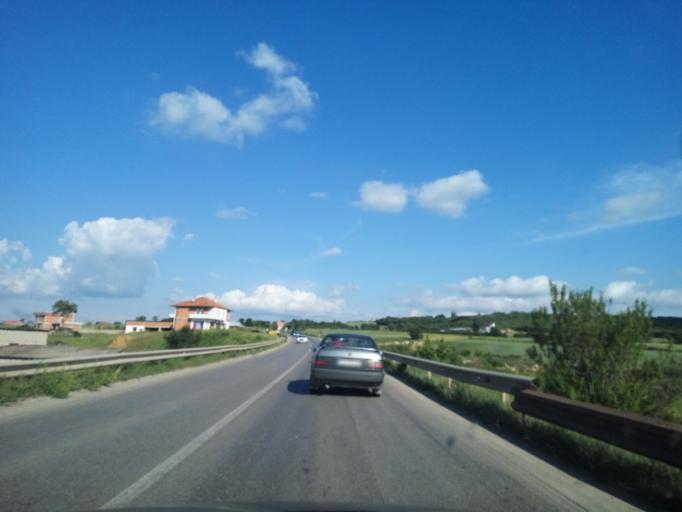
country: XK
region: Pec
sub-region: Komuna e Klines
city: Klina
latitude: 42.5888
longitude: 20.6690
